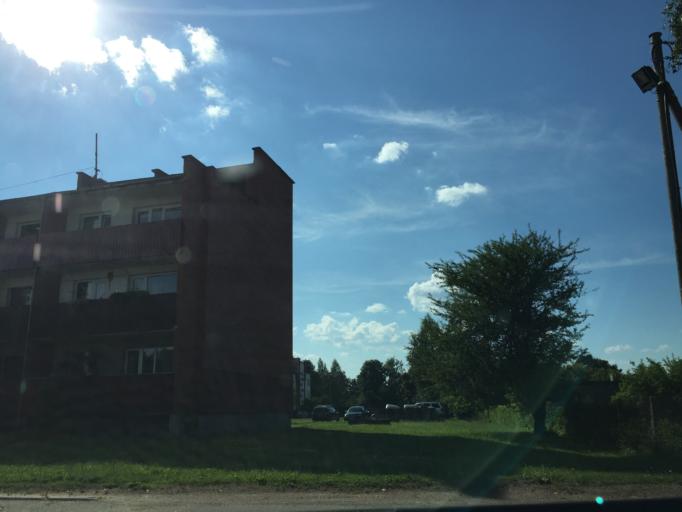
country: LV
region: Sigulda
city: Sigulda
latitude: 57.1601
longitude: 24.8650
